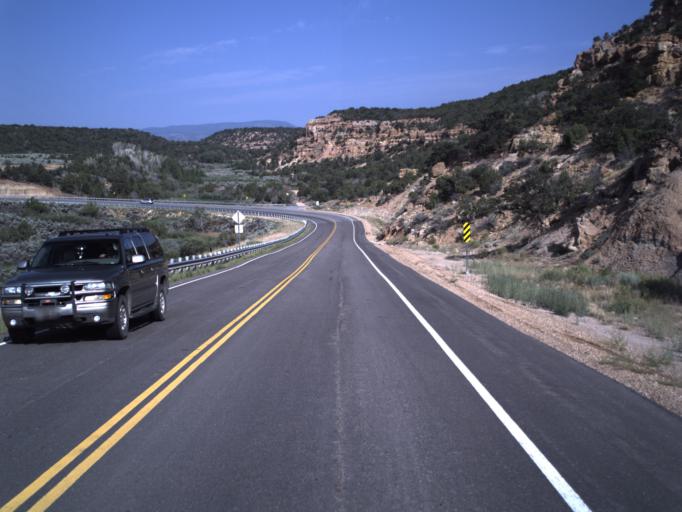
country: US
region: Utah
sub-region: Duchesne County
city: Duchesne
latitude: 40.3587
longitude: -110.3941
